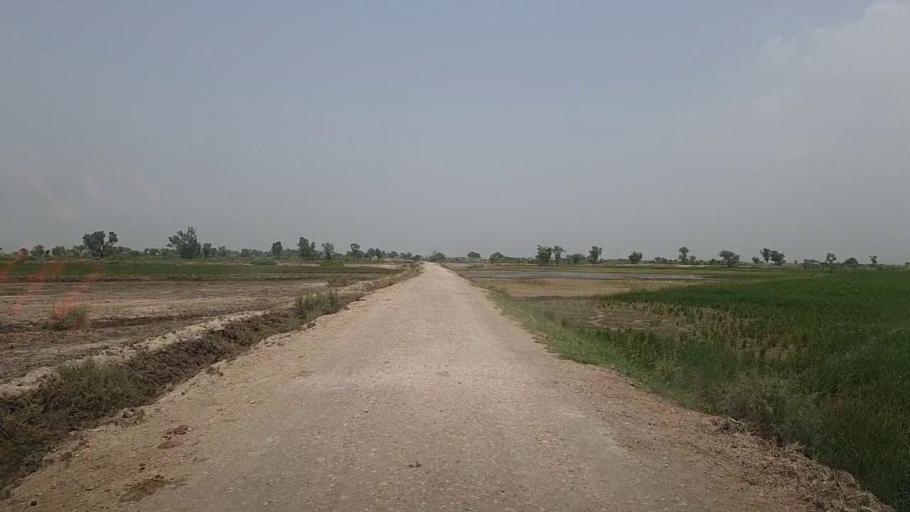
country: PK
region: Sindh
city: Sita Road
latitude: 27.0767
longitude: 67.8705
